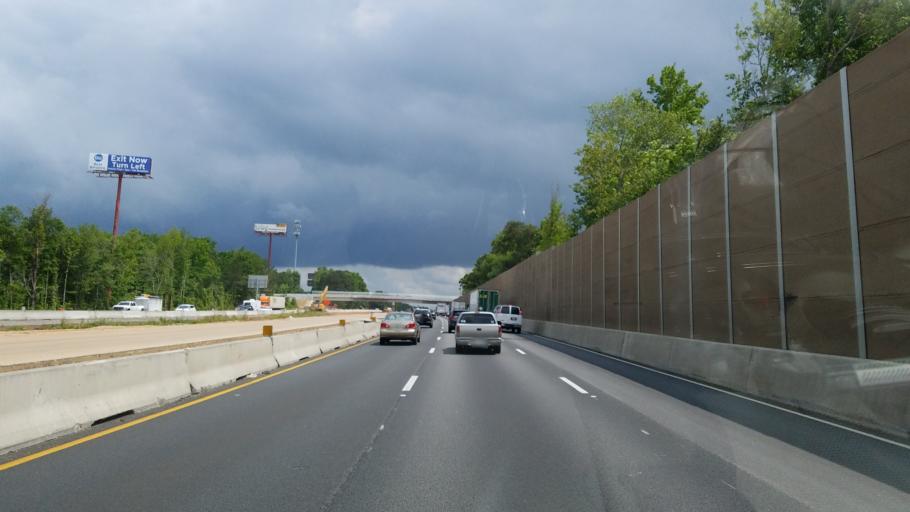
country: US
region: Georgia
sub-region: Henry County
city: McDonough
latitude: 33.4548
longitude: -84.2063
